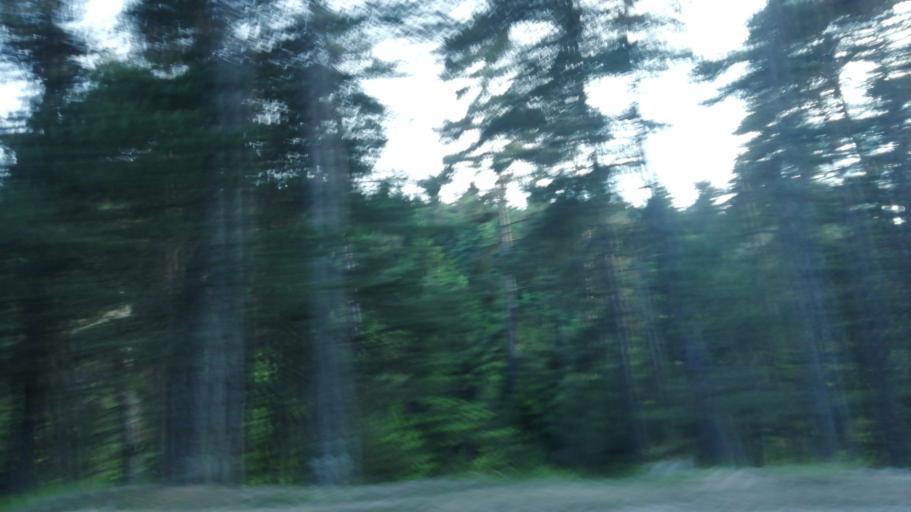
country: TR
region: Karabuk
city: Eskipazar
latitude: 41.0451
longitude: 32.5497
